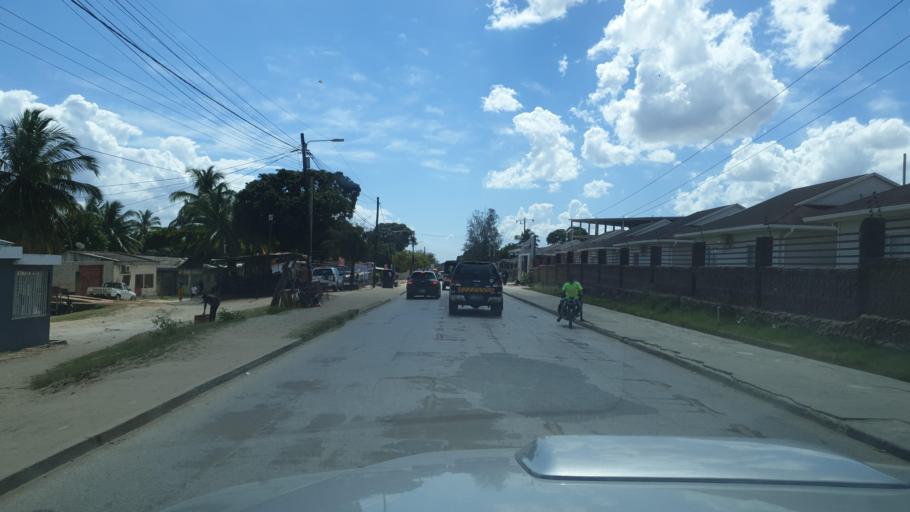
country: MZ
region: Nampula
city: Nacala
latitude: -14.5556
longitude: 40.6858
